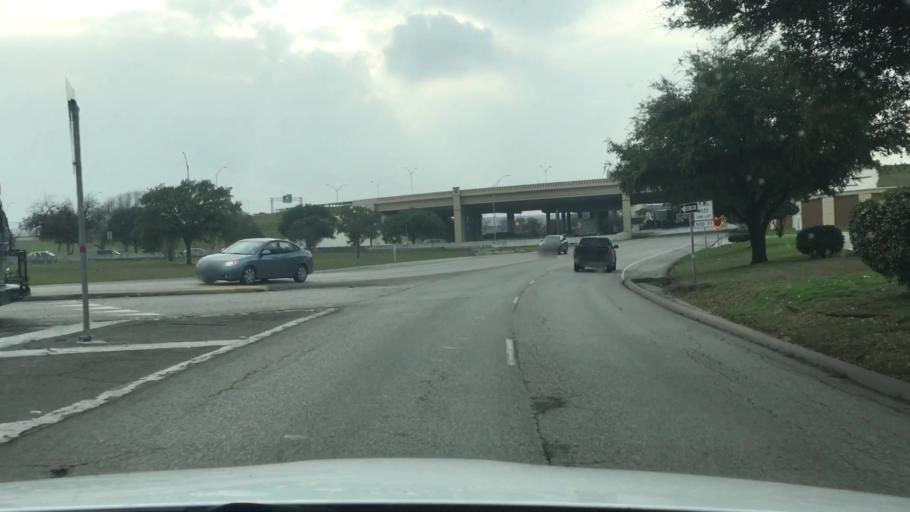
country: US
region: Texas
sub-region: Bexar County
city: Windcrest
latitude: 29.5236
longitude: -98.3915
